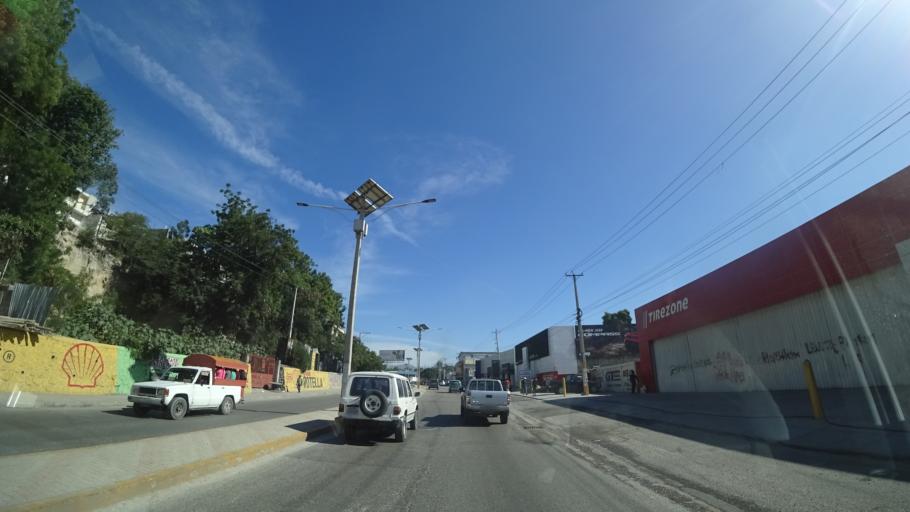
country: HT
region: Ouest
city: Delmas 73
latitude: 18.5568
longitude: -72.3165
